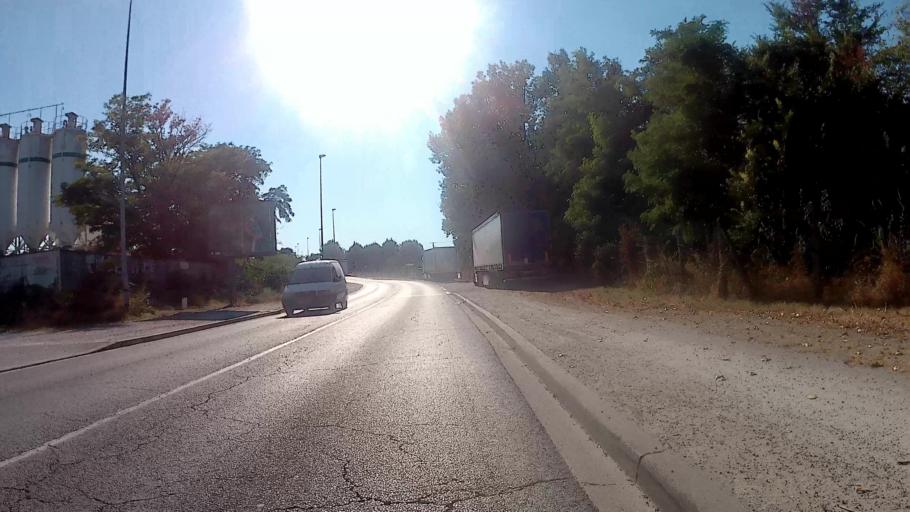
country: FR
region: Aquitaine
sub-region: Departement de la Gironde
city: Villenave-d'Ornon
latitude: 44.7821
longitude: -0.5381
